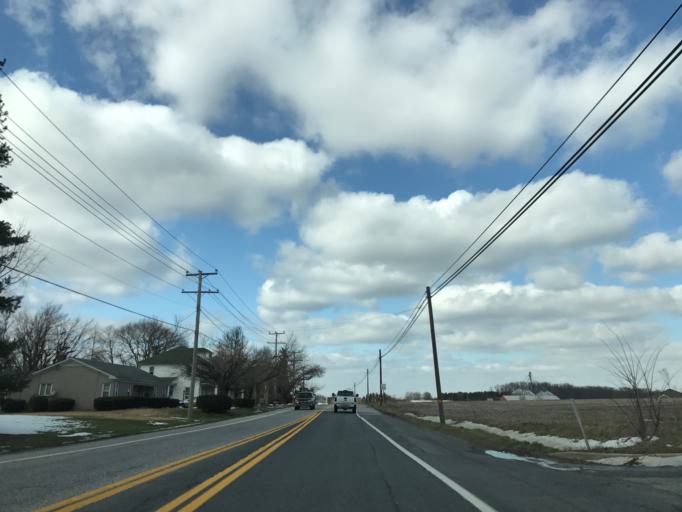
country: US
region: Maryland
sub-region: Carroll County
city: Westminster
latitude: 39.6178
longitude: -76.9970
